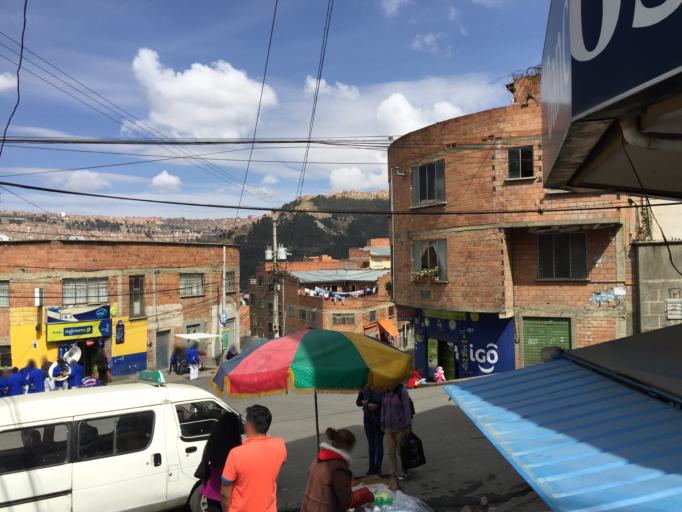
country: BO
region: La Paz
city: La Paz
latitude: -16.4815
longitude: -68.1399
